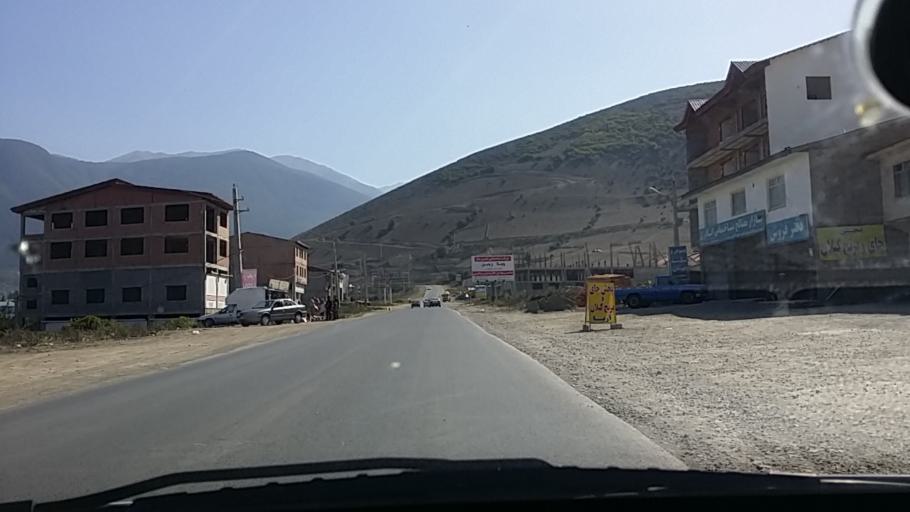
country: IR
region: Mazandaran
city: `Abbasabad
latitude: 36.5214
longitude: 51.1594
